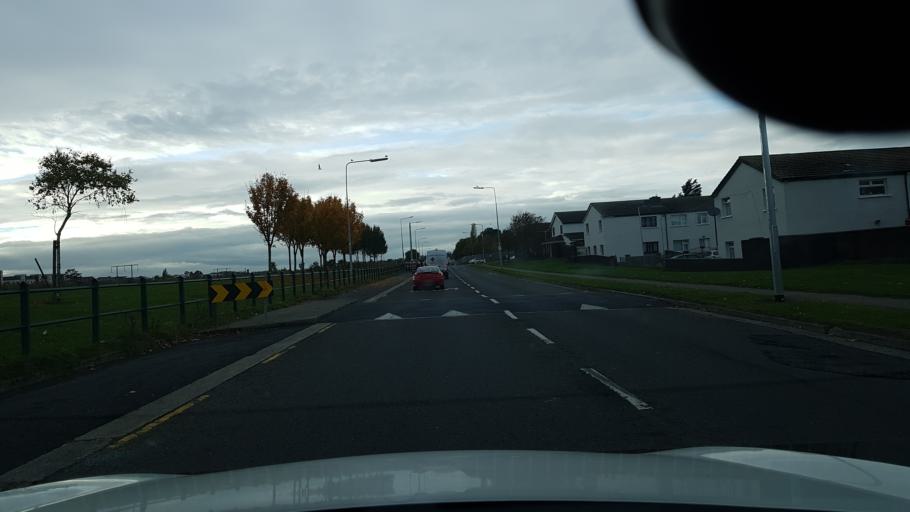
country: IE
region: Leinster
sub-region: Dublin City
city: Finglas
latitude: 53.3787
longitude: -6.3074
